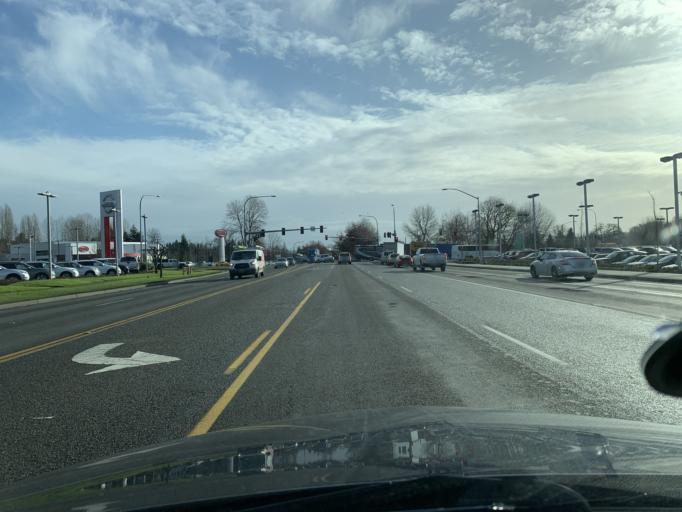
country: US
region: Washington
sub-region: Pierce County
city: North Puyallup
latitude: 47.2068
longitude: -122.2953
